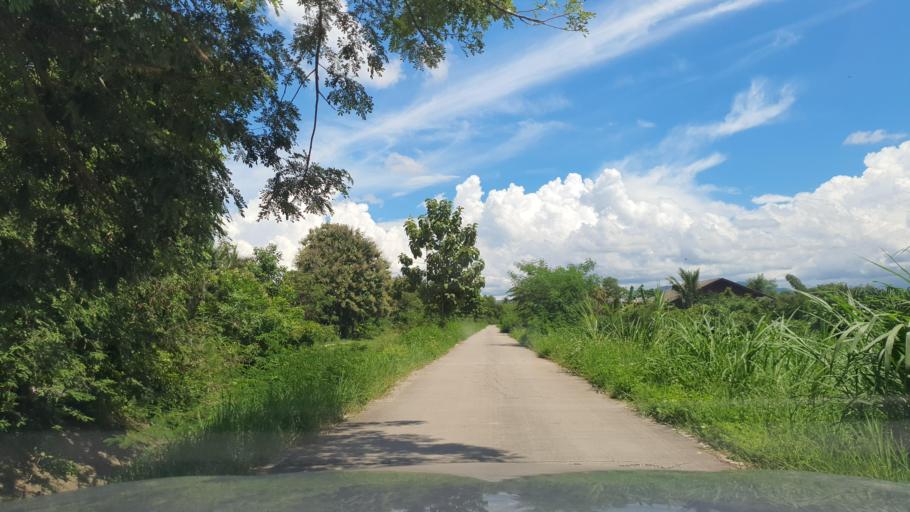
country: TH
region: Chiang Mai
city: San Kamphaeng
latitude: 18.7334
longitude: 99.1175
